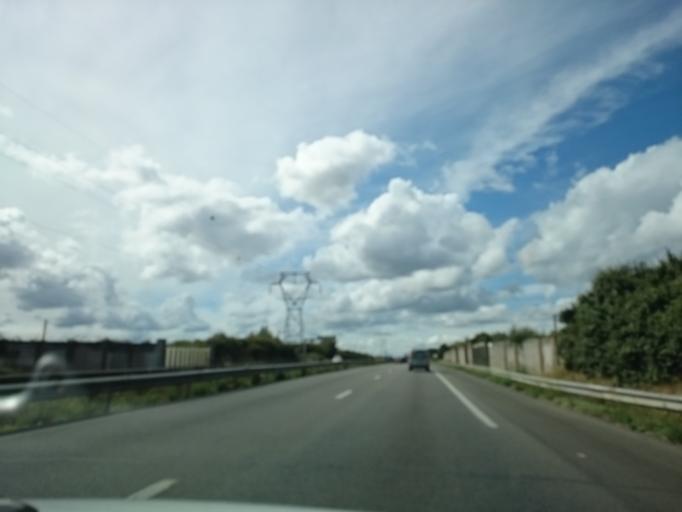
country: FR
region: Pays de la Loire
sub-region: Departement de la Loire-Atlantique
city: Reze
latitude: 47.1663
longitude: -1.5719
